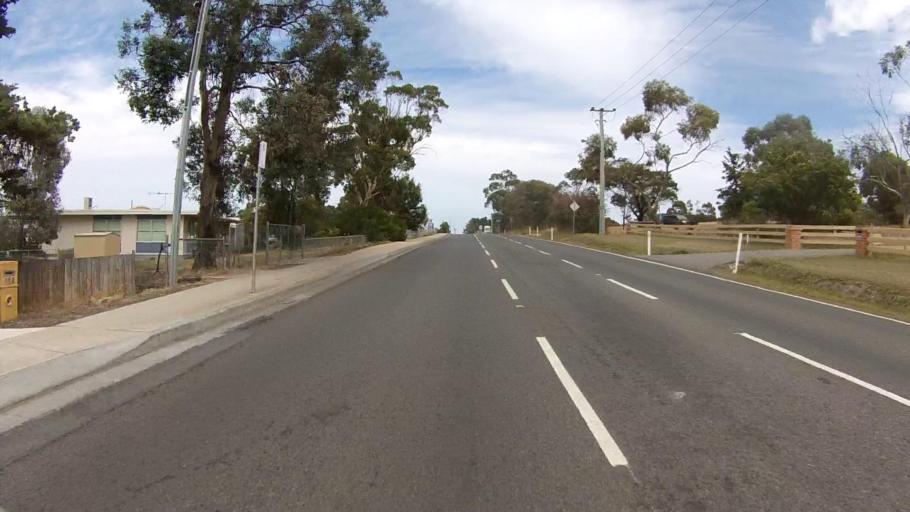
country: AU
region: Tasmania
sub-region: Clarence
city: Lauderdale
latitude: -42.9032
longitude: 147.4780
